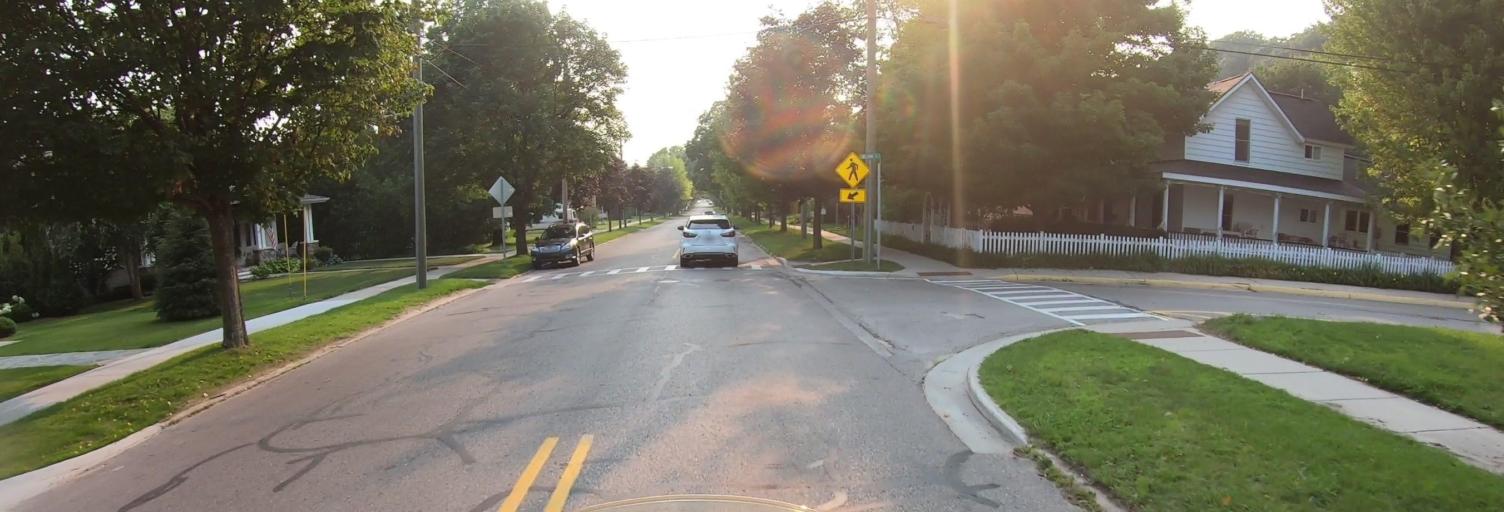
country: US
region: Michigan
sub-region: Emmet County
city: Harbor Springs
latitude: 45.4320
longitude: -84.9786
